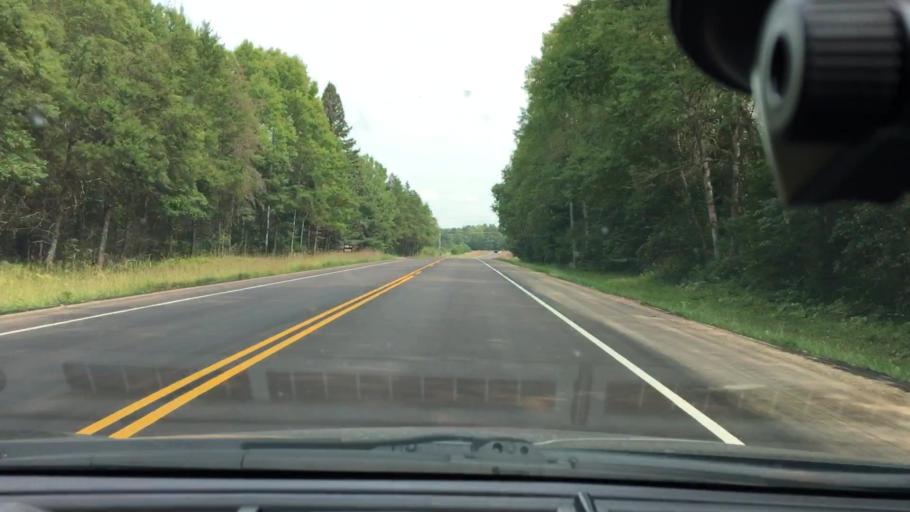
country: US
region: Minnesota
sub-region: Crow Wing County
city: Nisswa
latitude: 46.5298
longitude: -94.2380
